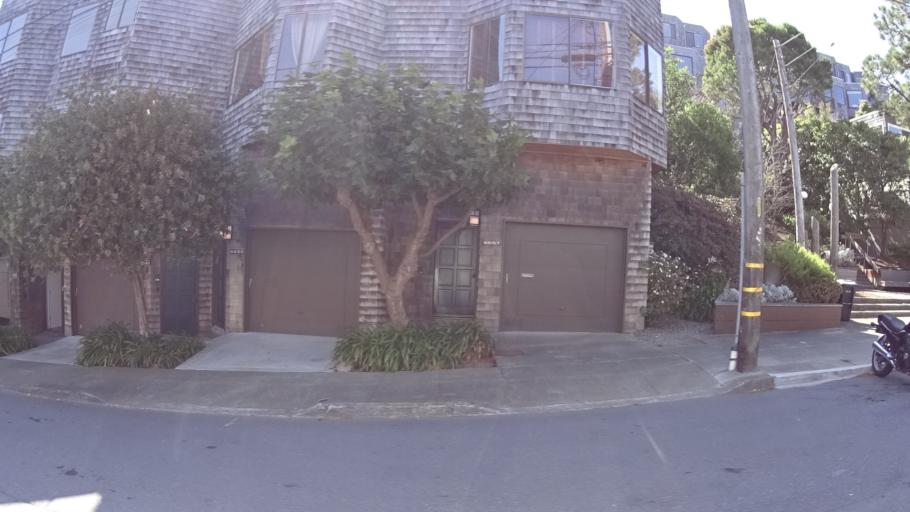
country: US
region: California
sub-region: San Francisco County
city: San Francisco
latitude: 37.7493
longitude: -122.4414
